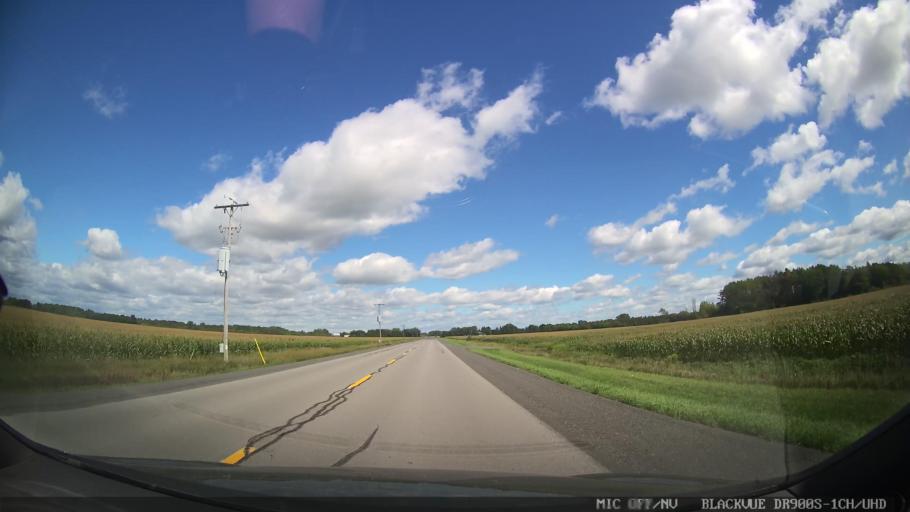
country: CA
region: Ontario
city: Bells Corners
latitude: 45.1793
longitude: -75.7569
